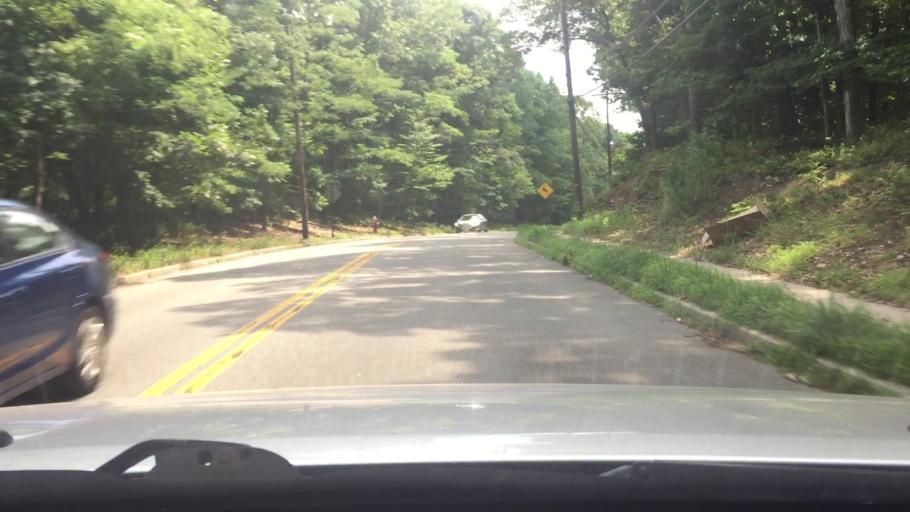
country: US
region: New Jersey
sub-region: Middlesex County
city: East Brunswick
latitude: 40.4106
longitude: -74.4073
